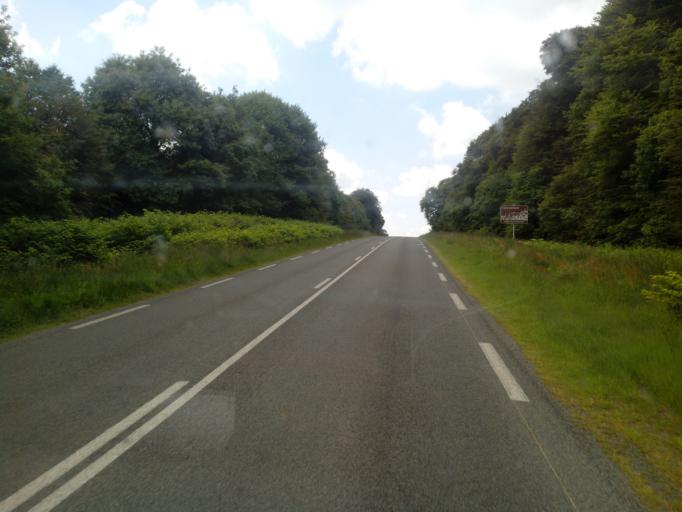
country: FR
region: Brittany
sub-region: Departement d'Ille-et-Vilaine
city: Landean
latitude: 48.3820
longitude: -1.1718
